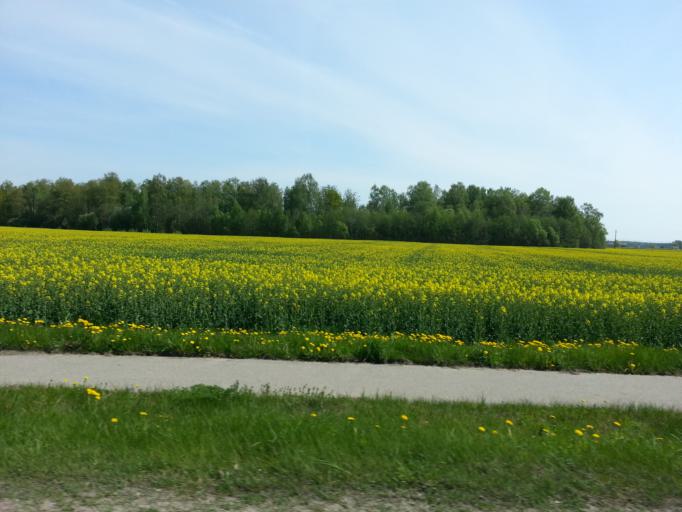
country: LT
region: Panevezys
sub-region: Panevezys City
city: Panevezys
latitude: 55.7719
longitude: 24.2952
